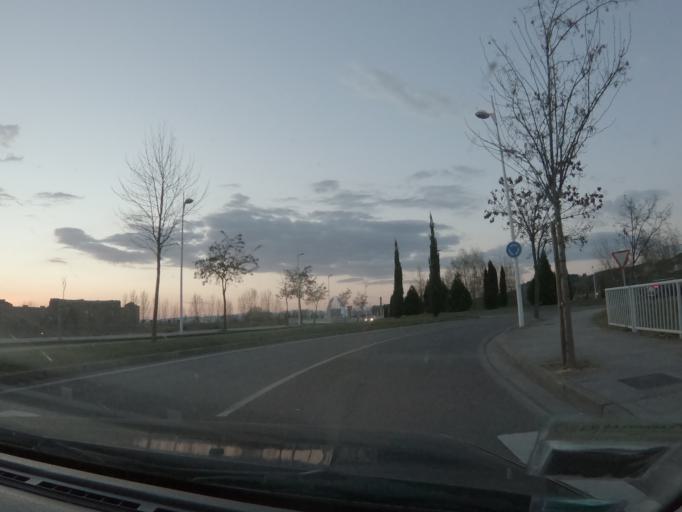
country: ES
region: Castille and Leon
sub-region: Provincia de Leon
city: Ponferrada
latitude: 42.5547
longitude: -6.5885
